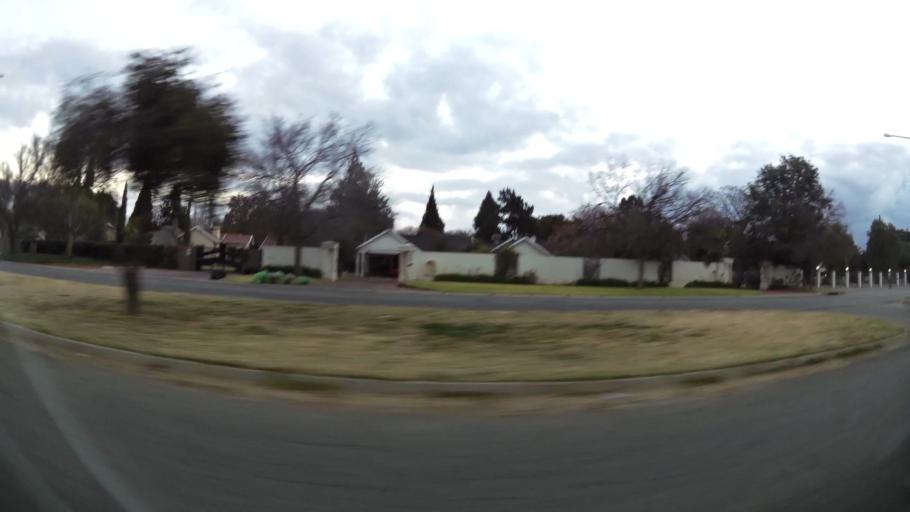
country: ZA
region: Orange Free State
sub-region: Lejweleputswa District Municipality
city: Welkom
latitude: -27.9695
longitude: 26.7328
